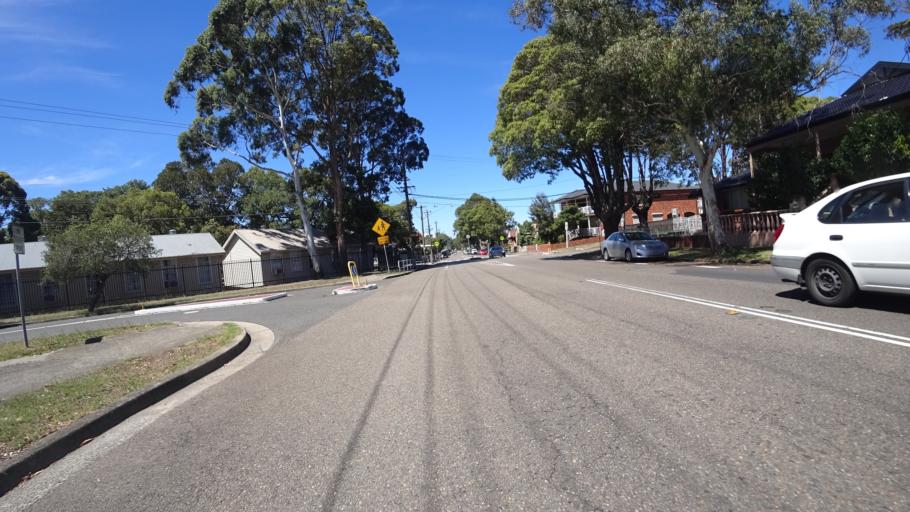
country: AU
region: New South Wales
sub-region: Rockdale
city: Bardwell Valley
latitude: -33.9382
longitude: 151.1388
